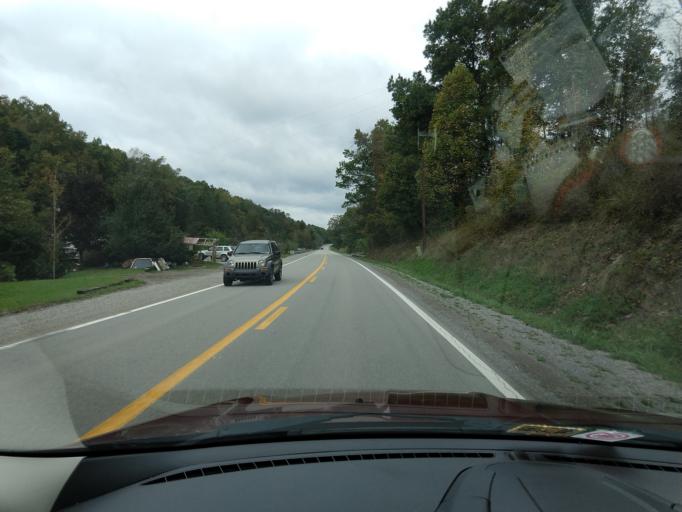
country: US
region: West Virginia
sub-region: Barbour County
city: Belington
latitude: 39.0450
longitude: -79.9569
